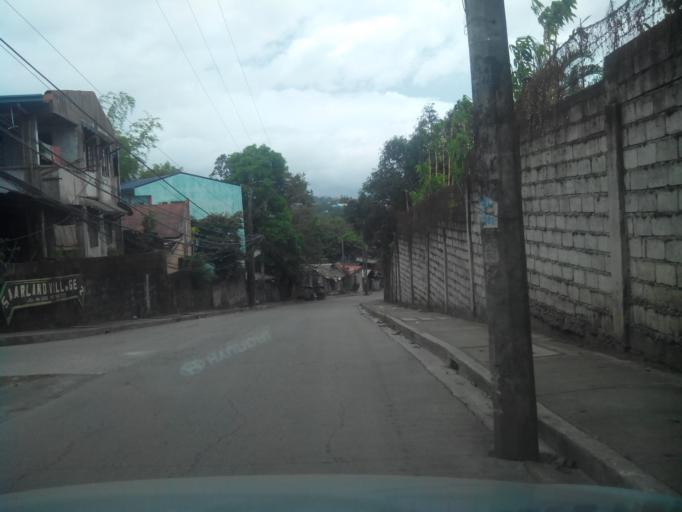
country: PH
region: Calabarzon
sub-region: Province of Rizal
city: Teresa
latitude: 14.5929
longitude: 121.1802
